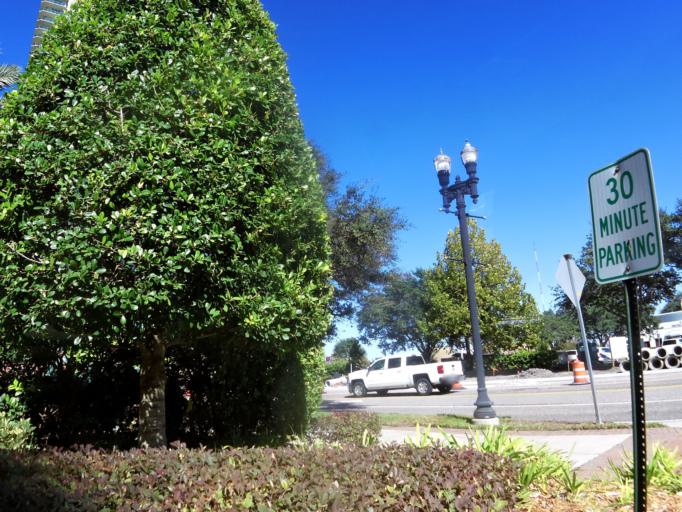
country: US
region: Florida
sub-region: Duval County
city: Jacksonville
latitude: 30.3176
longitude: -81.6550
